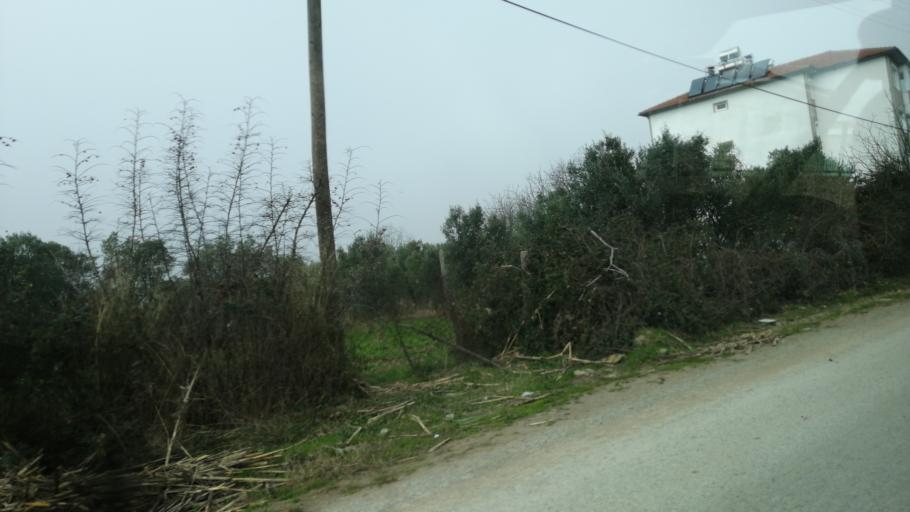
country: TR
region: Yalova
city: Cinarcik
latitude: 40.6372
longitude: 29.0786
